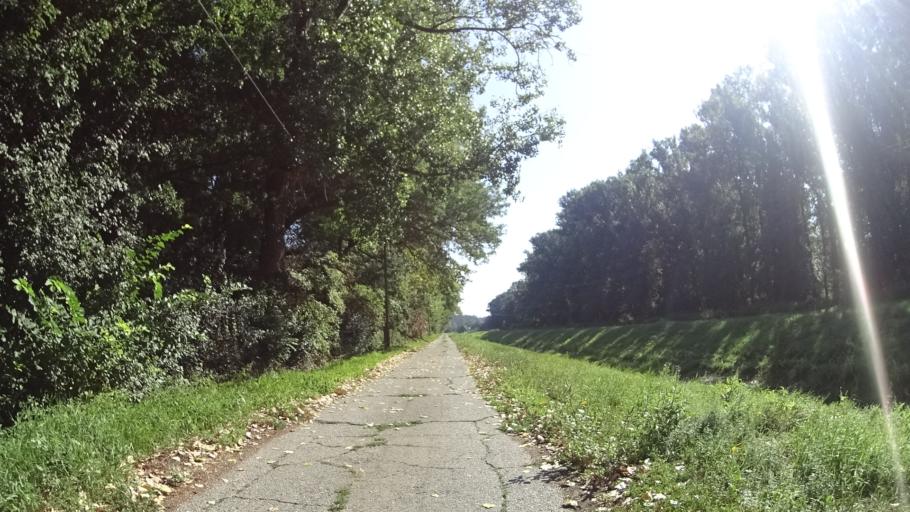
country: CZ
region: South Moravian
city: Hodonin
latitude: 48.8141
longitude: 17.1110
